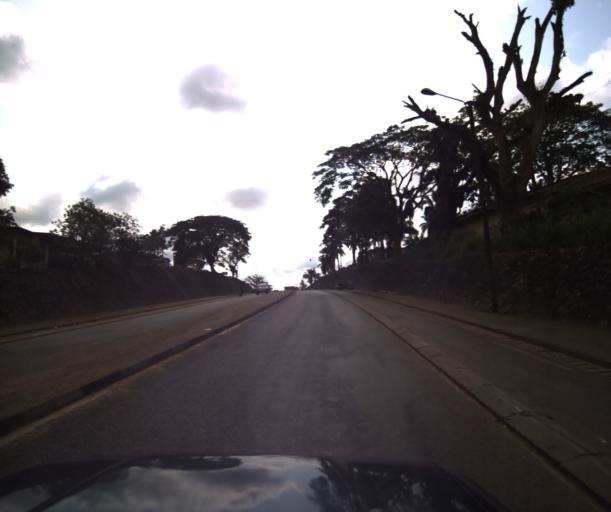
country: CM
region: Littoral
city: Edea
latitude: 3.7920
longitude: 10.1351
